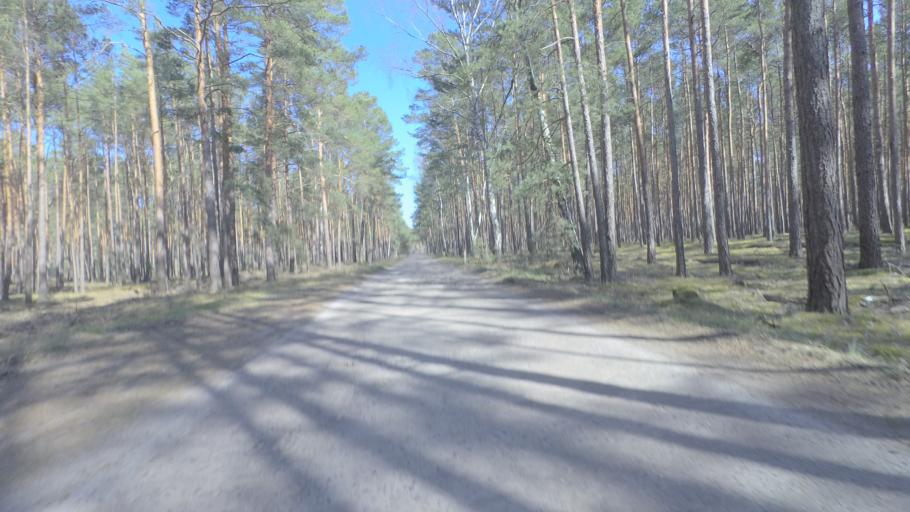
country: DE
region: Brandenburg
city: Gross Koris
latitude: 52.1751
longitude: 13.7289
